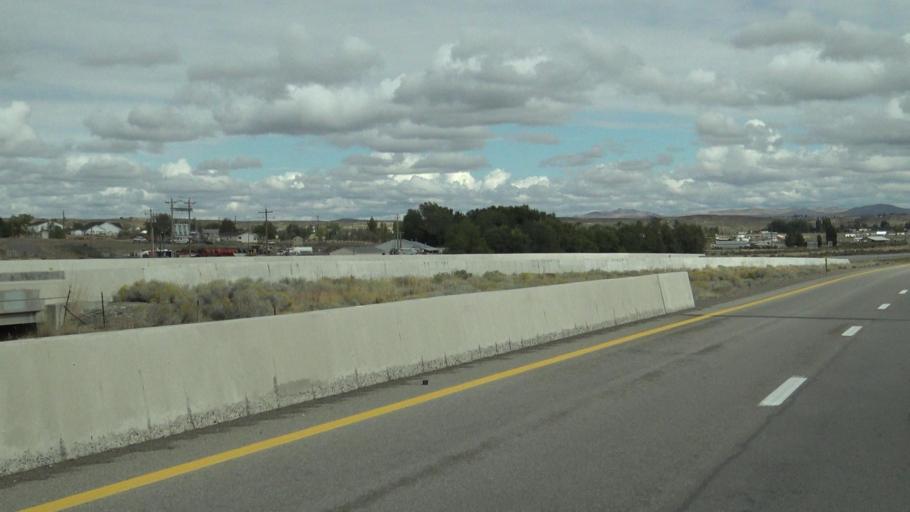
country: US
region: Nevada
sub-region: Elko County
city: Elko
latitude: 40.9337
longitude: -115.6654
